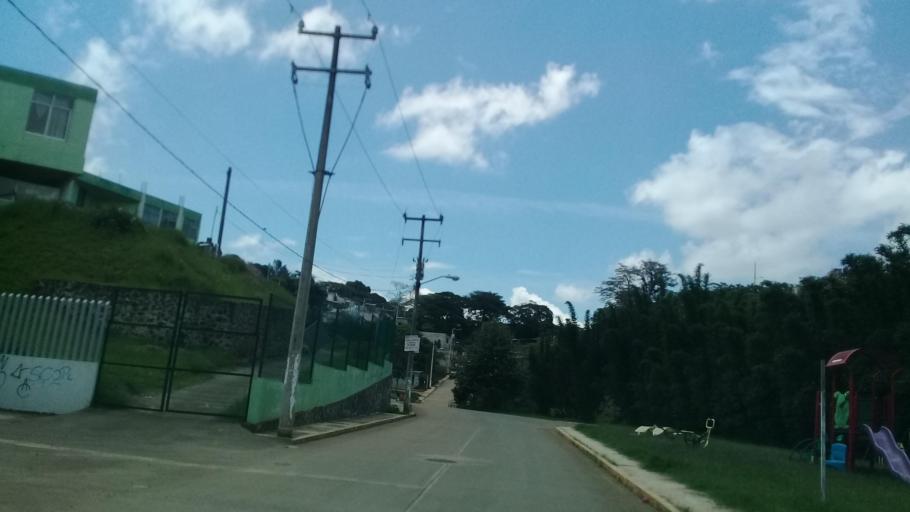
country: MX
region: Veracruz
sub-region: Xalapa
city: Fraccionamiento las Fuentes
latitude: 19.4994
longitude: -96.8836
